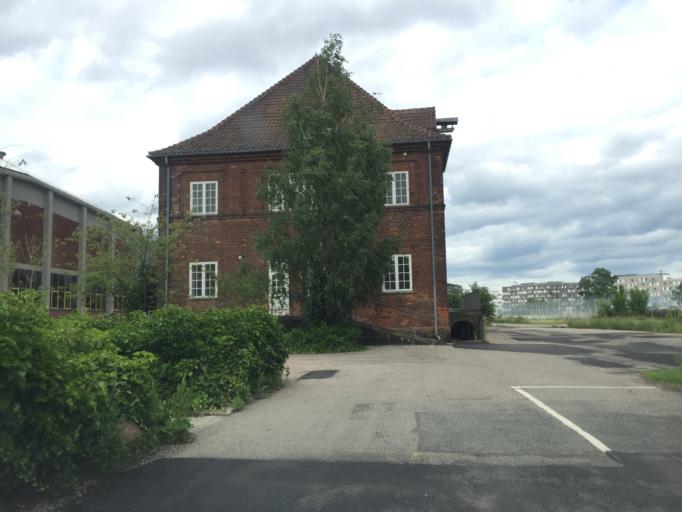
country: DK
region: Capital Region
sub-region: Kobenhavn
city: Copenhagen
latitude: 55.6601
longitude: 12.5520
